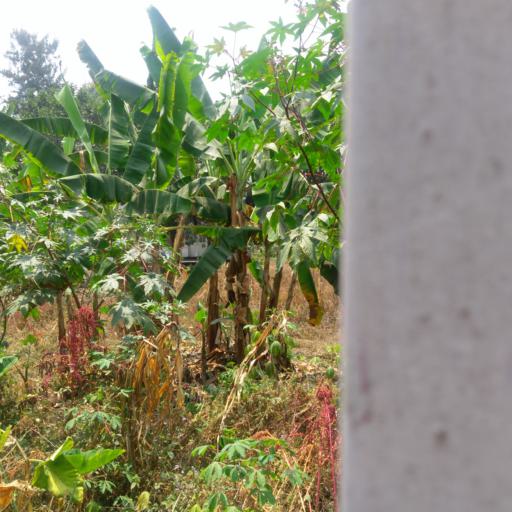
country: RW
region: Western Province
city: Gisenyi
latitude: -1.6963
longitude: 29.2354
